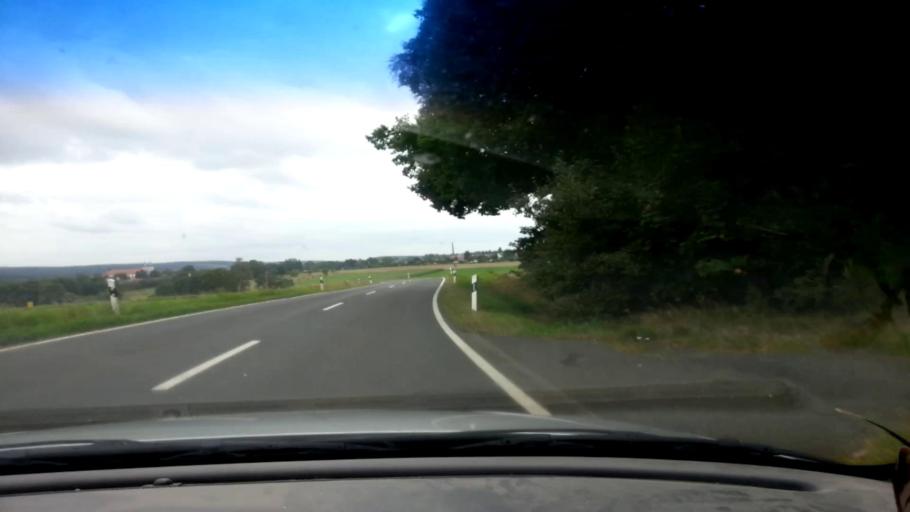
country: DE
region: Bavaria
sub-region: Upper Palatinate
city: Waldsassen
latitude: 50.0155
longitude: 12.3113
